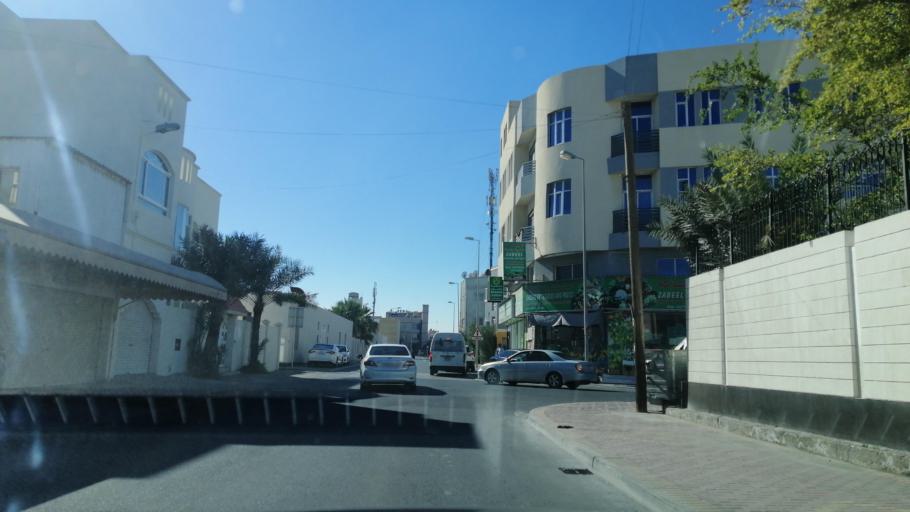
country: BH
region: Muharraq
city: Al Hadd
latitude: 26.2366
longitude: 50.6540
